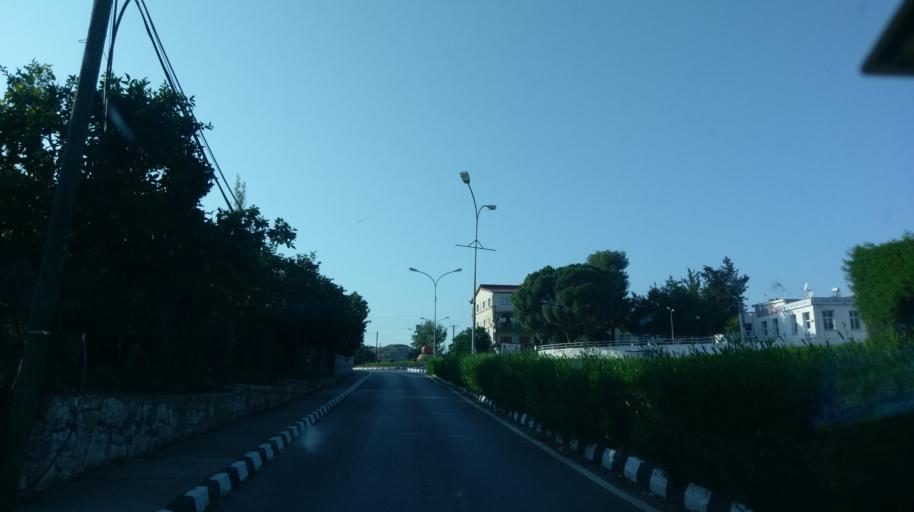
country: CY
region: Lefkosia
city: Lefka
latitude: 35.1175
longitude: 32.8511
